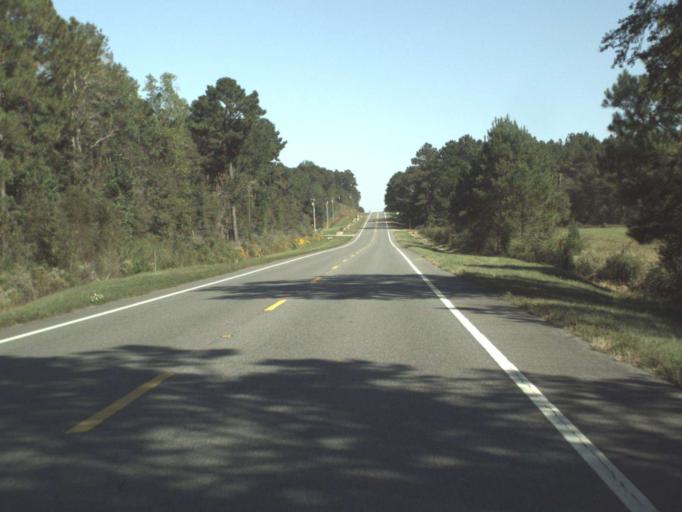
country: US
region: Florida
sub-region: Walton County
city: DeFuniak Springs
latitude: 30.8331
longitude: -85.9536
